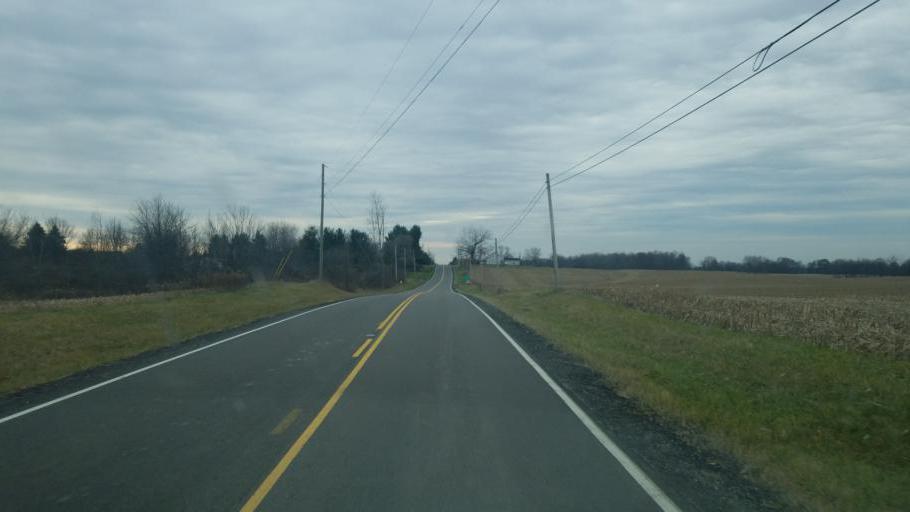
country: US
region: Ohio
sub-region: Knox County
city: Centerburg
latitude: 40.3380
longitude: -82.6905
